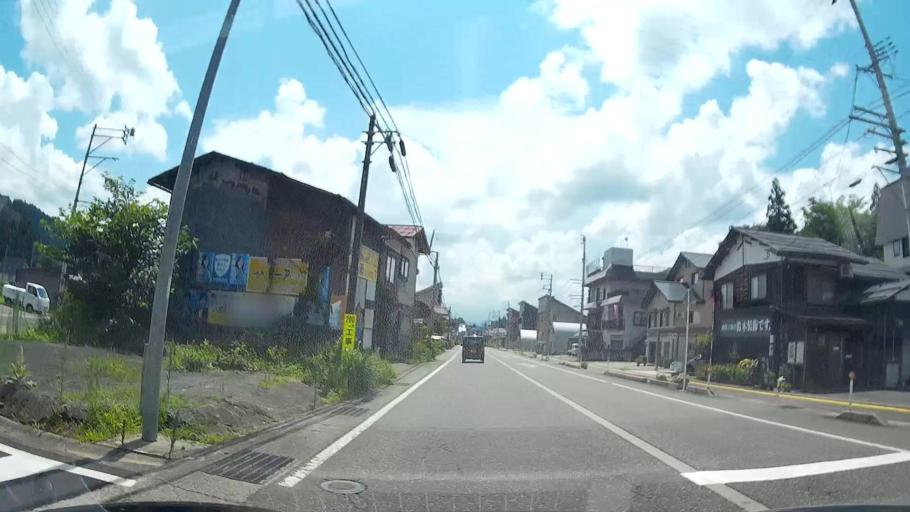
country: JP
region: Niigata
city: Tokamachi
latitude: 37.0797
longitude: 138.7199
